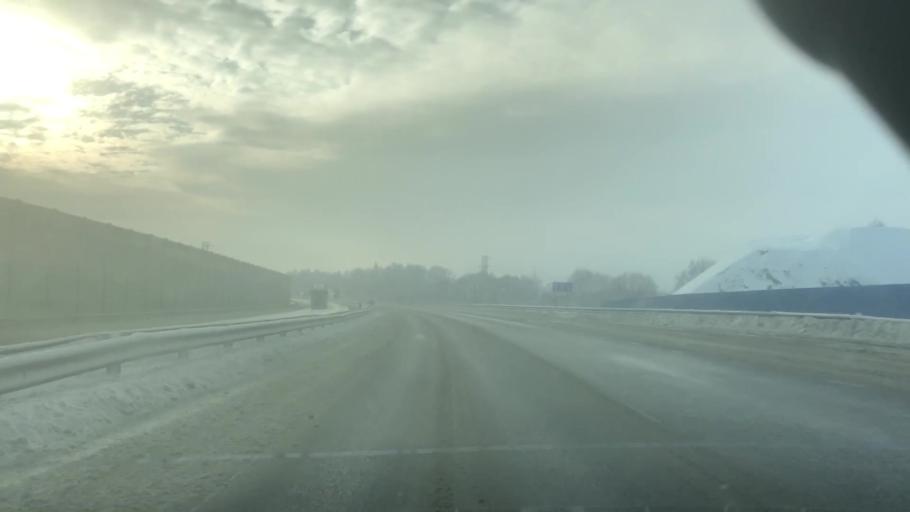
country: RU
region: Tula
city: Venev
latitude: 54.3925
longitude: 38.1546
